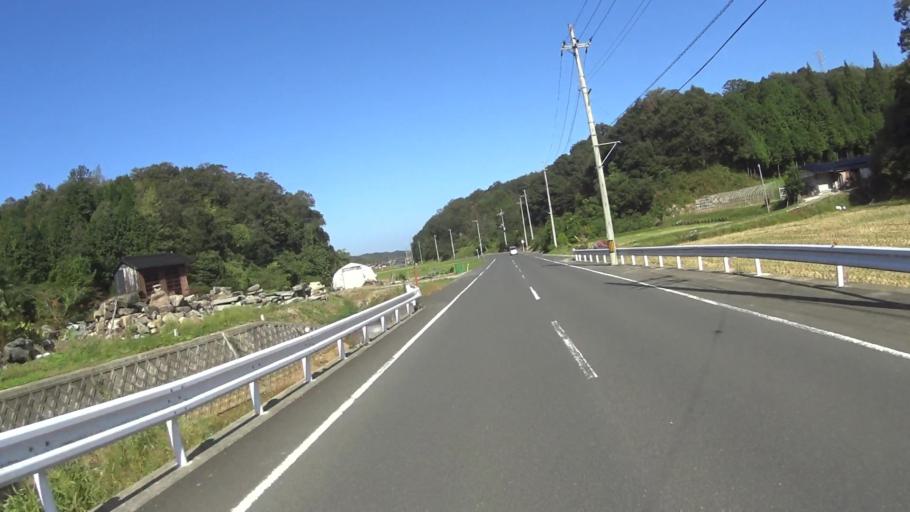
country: JP
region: Kyoto
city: Miyazu
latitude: 35.6688
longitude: 135.0581
